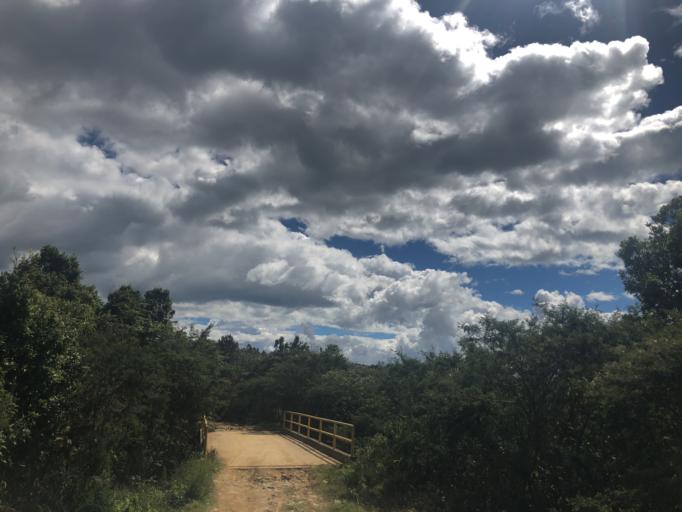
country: CO
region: Cauca
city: Silvia
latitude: 2.6818
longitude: -76.4357
